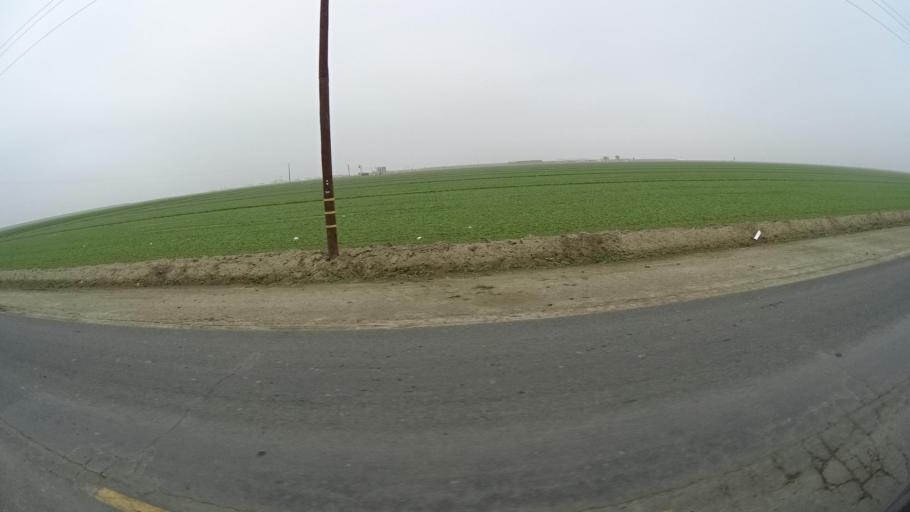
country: US
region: California
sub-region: Kern County
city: Wasco
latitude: 35.7175
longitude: -119.4275
